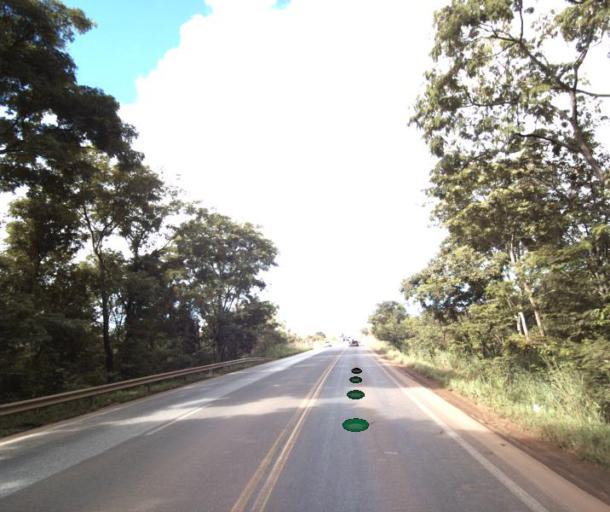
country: BR
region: Goias
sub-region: Uruacu
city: Uruacu
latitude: -14.5710
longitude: -49.1566
